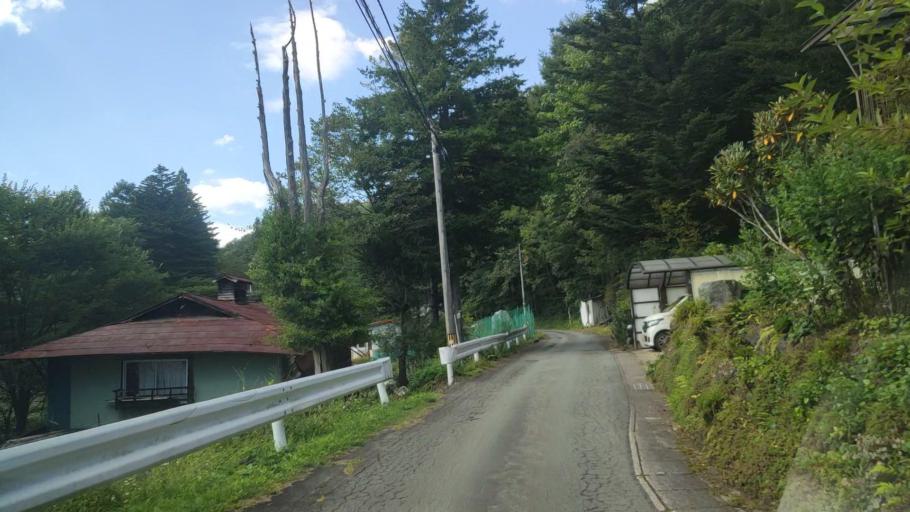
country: JP
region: Gunma
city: Nakanojomachi
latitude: 36.6571
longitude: 138.6238
